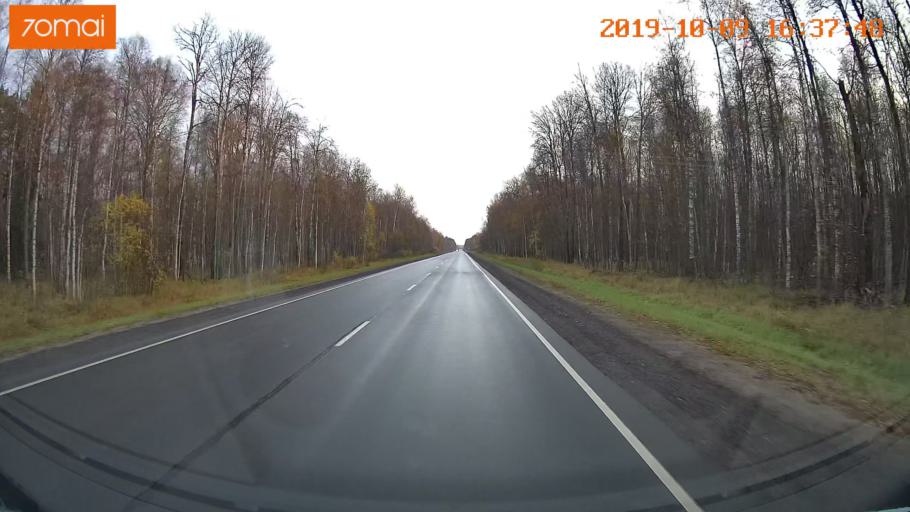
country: RU
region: Kostroma
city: Volgorechensk
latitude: 57.5215
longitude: 41.0291
